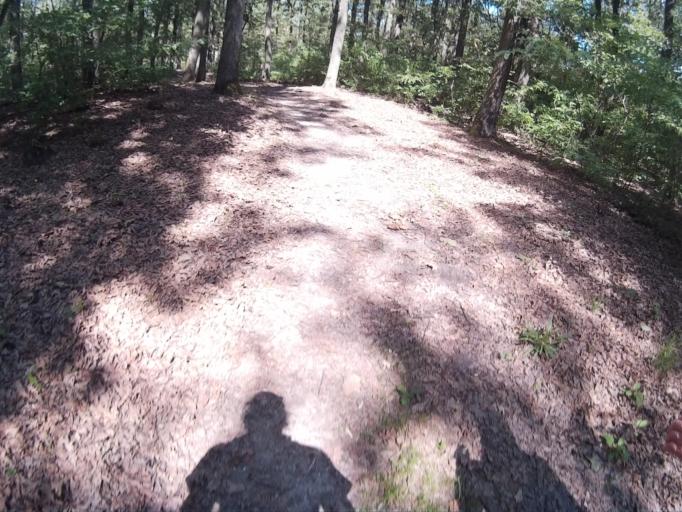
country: HU
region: Vas
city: Szombathely
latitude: 47.2216
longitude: 16.5528
